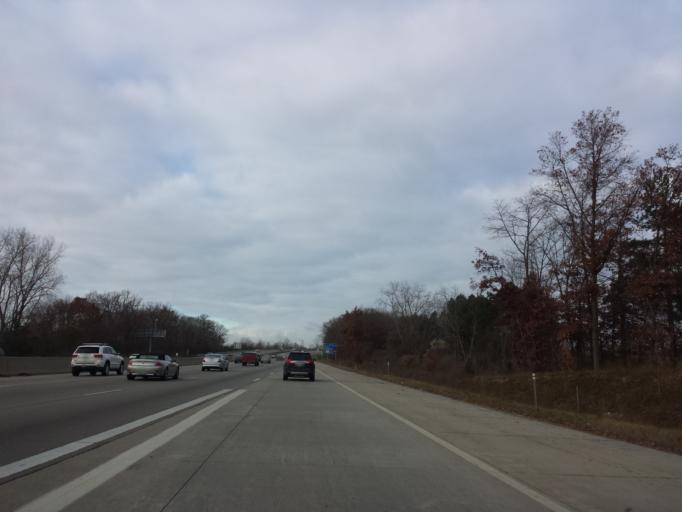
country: US
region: Michigan
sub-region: Oakland County
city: Rochester Hills
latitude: 42.6442
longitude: -83.1804
